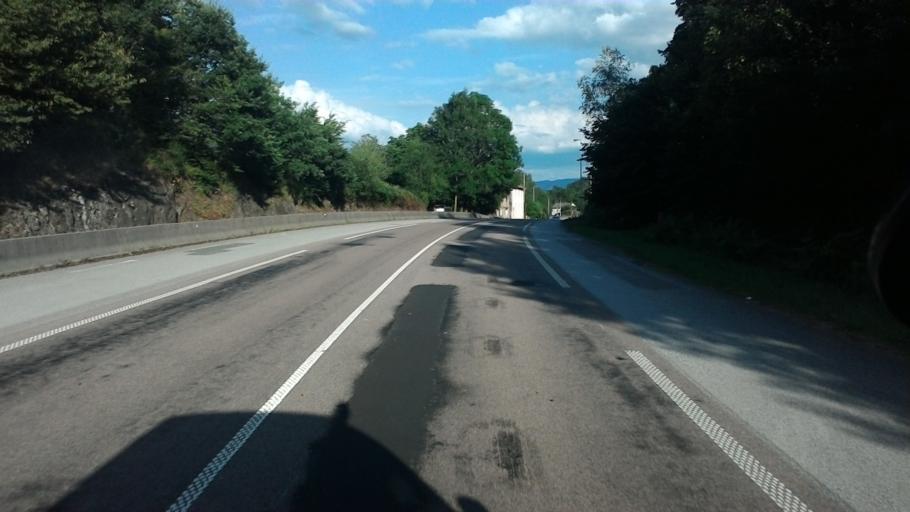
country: FR
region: Lorraine
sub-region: Departement des Vosges
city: Rupt-sur-Moselle
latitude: 47.9113
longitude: 6.6858
